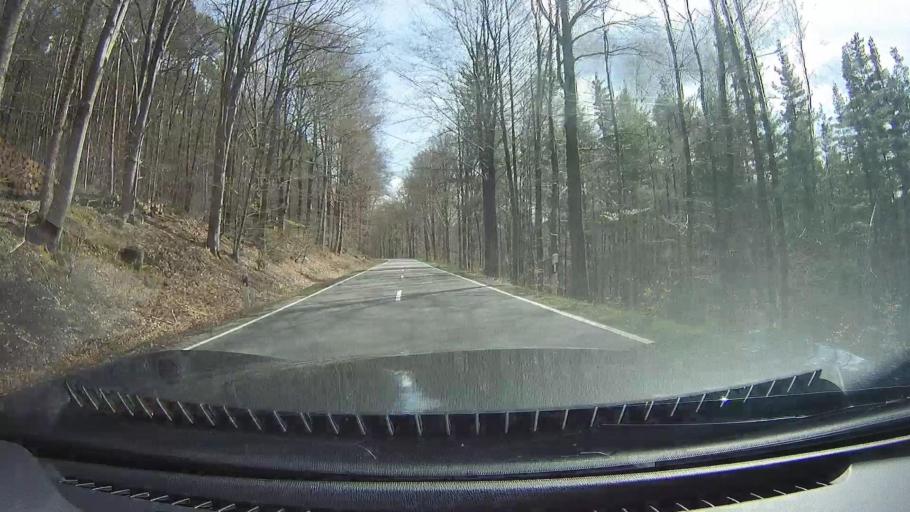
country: DE
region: Hesse
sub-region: Regierungsbezirk Darmstadt
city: Beerfelden
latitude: 49.5848
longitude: 9.0074
